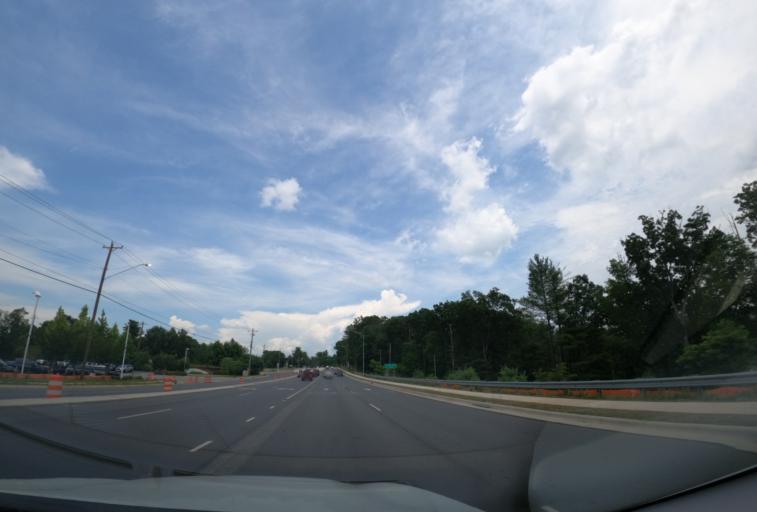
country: US
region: North Carolina
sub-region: Buncombe County
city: Bent Creek
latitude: 35.5360
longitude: -82.6001
